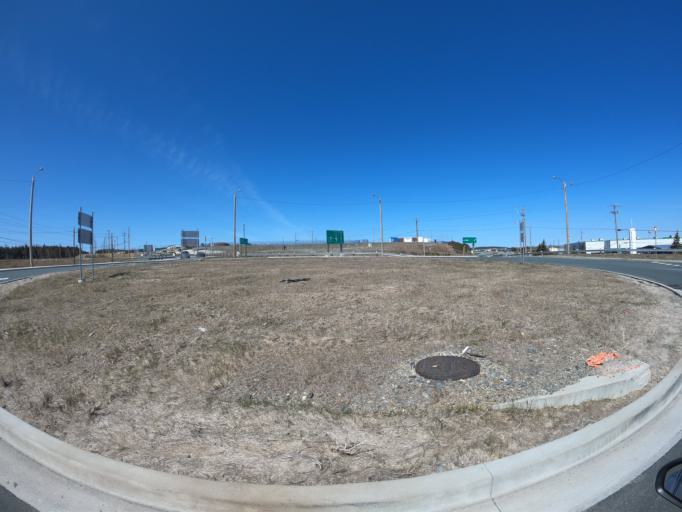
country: CA
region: Newfoundland and Labrador
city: Mount Pearl
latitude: 47.5084
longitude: -52.8227
